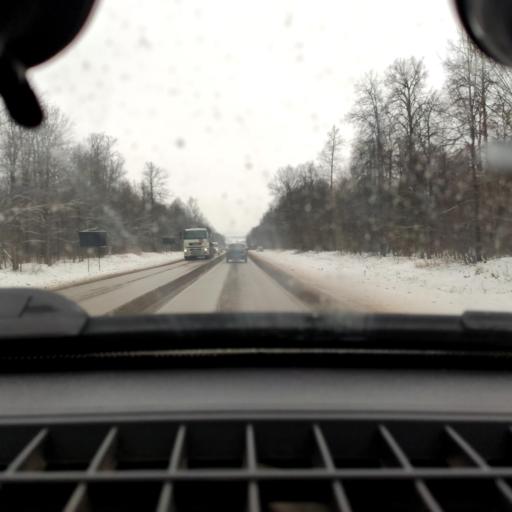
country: RU
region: Bashkortostan
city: Iglino
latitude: 54.7715
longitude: 56.4145
